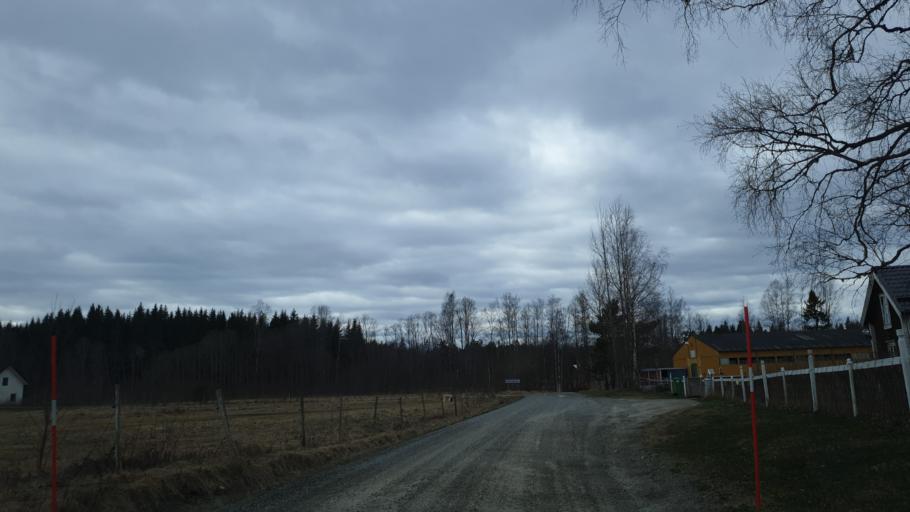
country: SE
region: OErebro
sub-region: Nora Kommun
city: As
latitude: 59.6009
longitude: 14.9084
